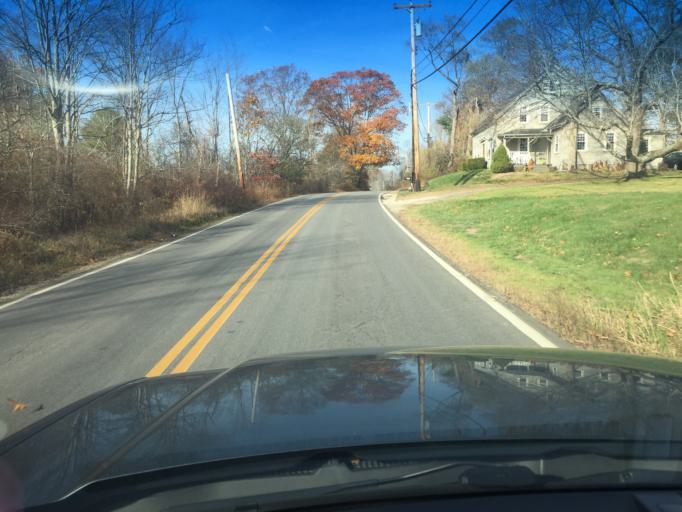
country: US
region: Maine
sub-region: York County
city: Eliot
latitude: 43.1781
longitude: -70.7270
